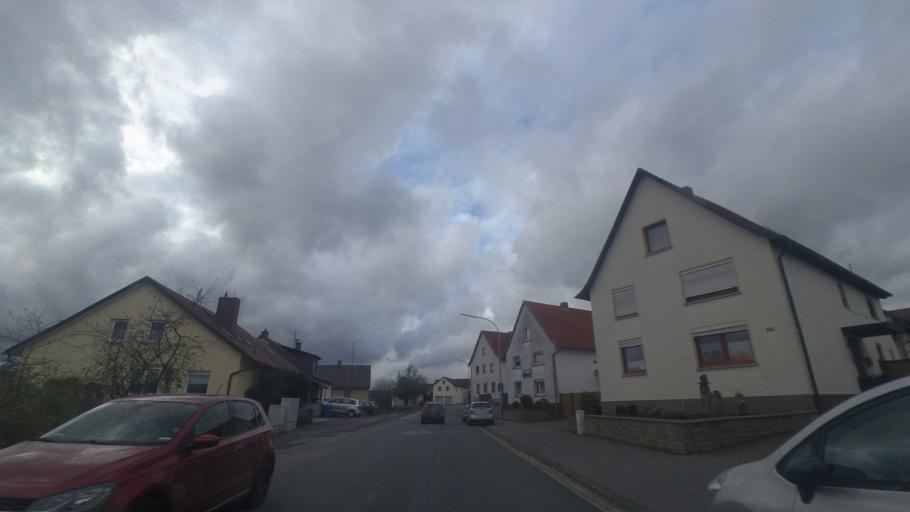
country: DE
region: Bavaria
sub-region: Regierungsbezirk Unterfranken
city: Bad Neustadt an der Saale
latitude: 50.3309
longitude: 10.1981
